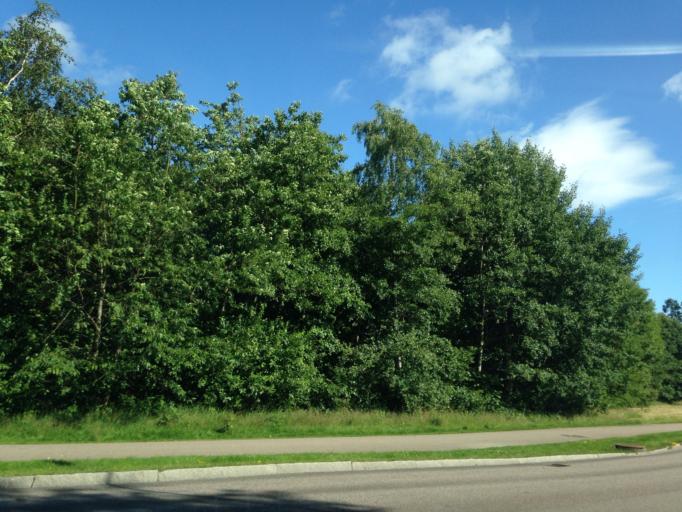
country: SE
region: Vaestra Goetaland
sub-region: Ale Kommun
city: Surte
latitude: 57.8092
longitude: 11.9762
